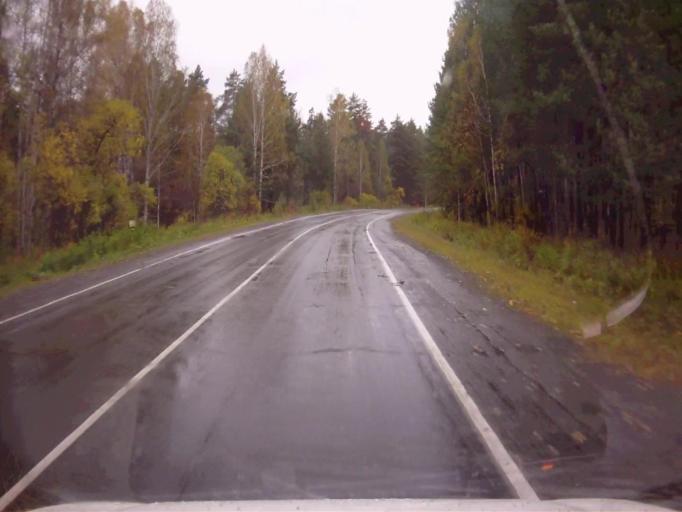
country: RU
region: Chelyabinsk
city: Verkhniy Ufaley
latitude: 55.9594
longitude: 60.3844
